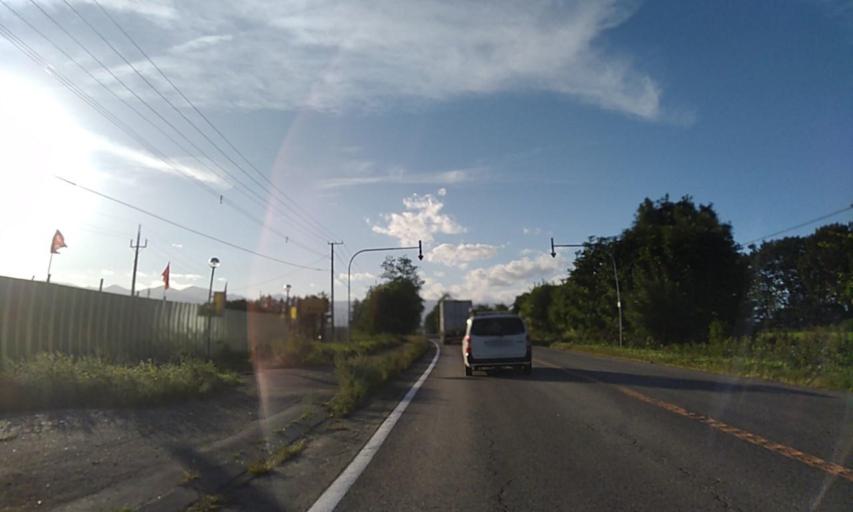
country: JP
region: Hokkaido
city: Obihiro
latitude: 42.9333
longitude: 142.9744
